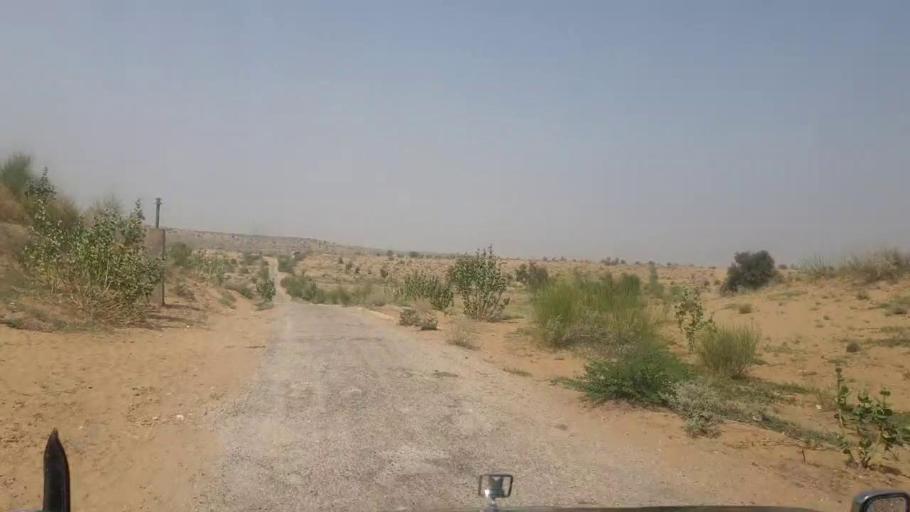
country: PK
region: Sindh
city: Islamkot
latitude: 25.1760
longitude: 70.2002
